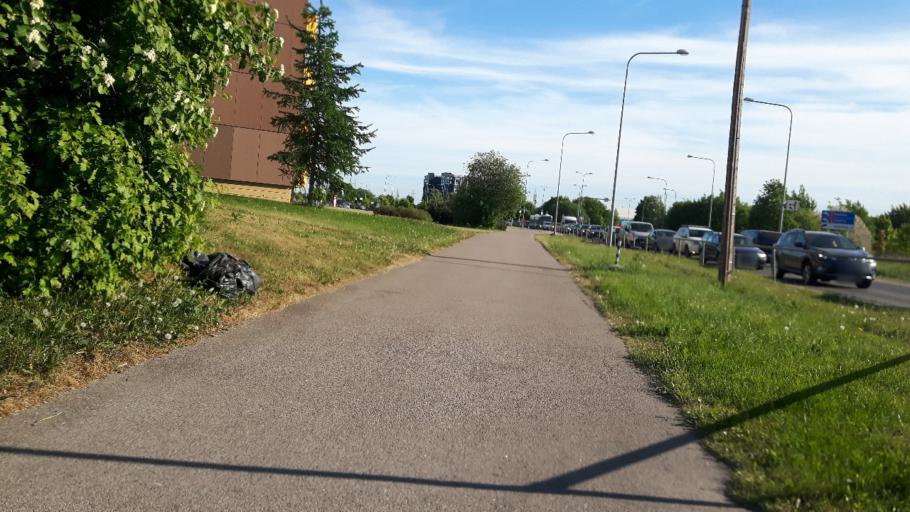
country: EE
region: Harju
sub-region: Tallinna linn
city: Kose
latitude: 59.4531
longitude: 24.8598
